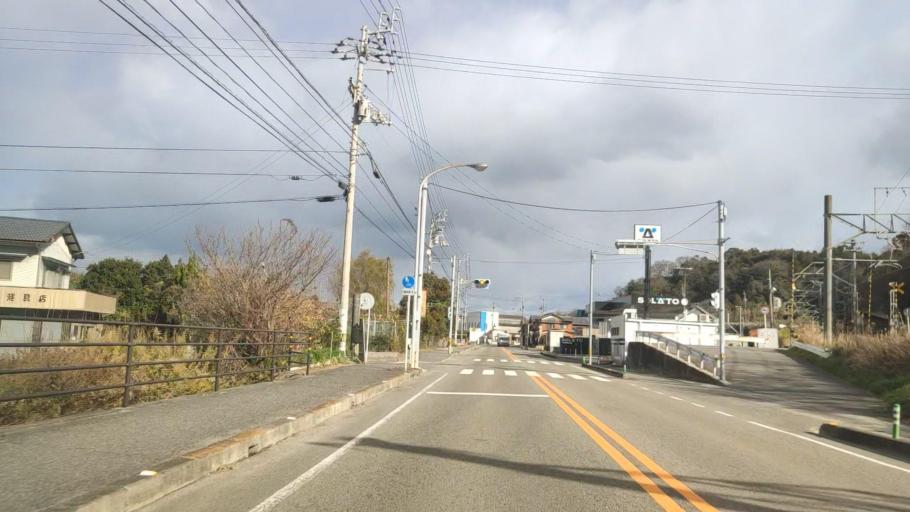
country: JP
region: Ehime
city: Hojo
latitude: 34.0406
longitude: 132.8480
